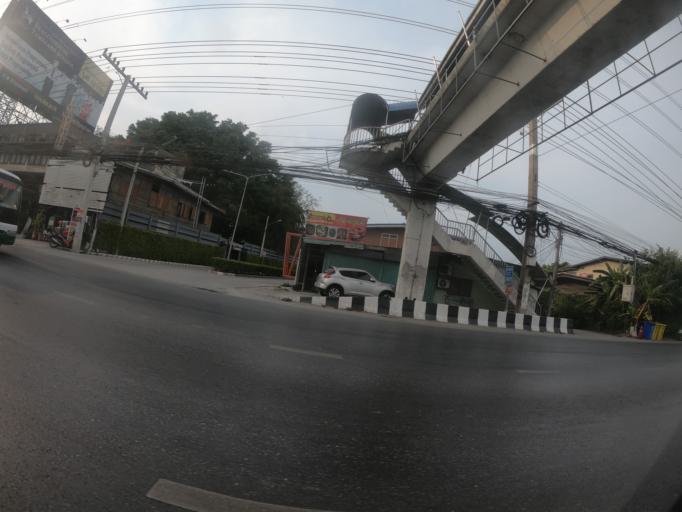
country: TH
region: Bangkok
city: Sai Mai
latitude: 13.9861
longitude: 100.6223
